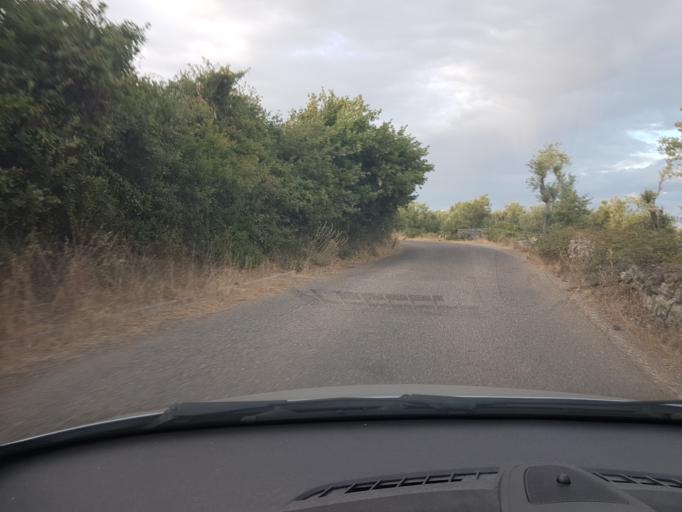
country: IT
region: Sardinia
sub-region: Provincia di Oristano
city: Seneghe
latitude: 40.0899
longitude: 8.6197
